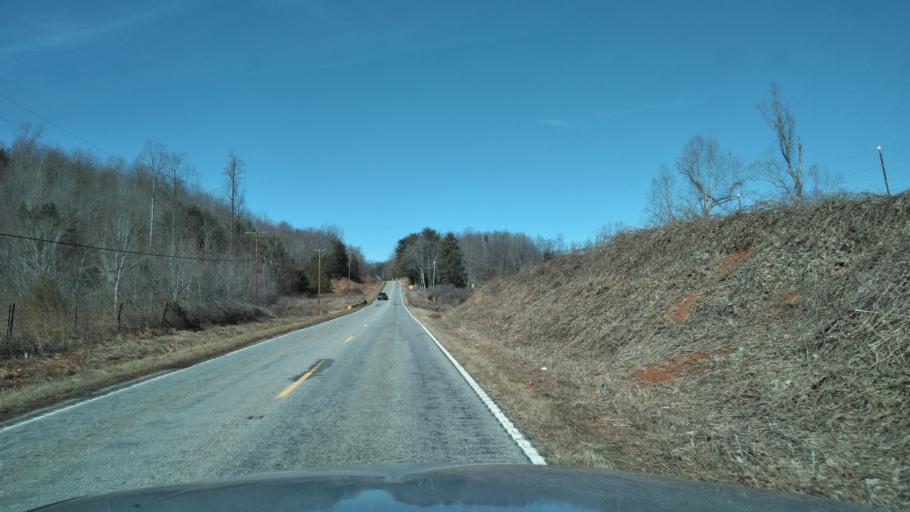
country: US
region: North Carolina
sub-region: Polk County
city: Columbus
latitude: 35.3161
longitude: -82.1735
